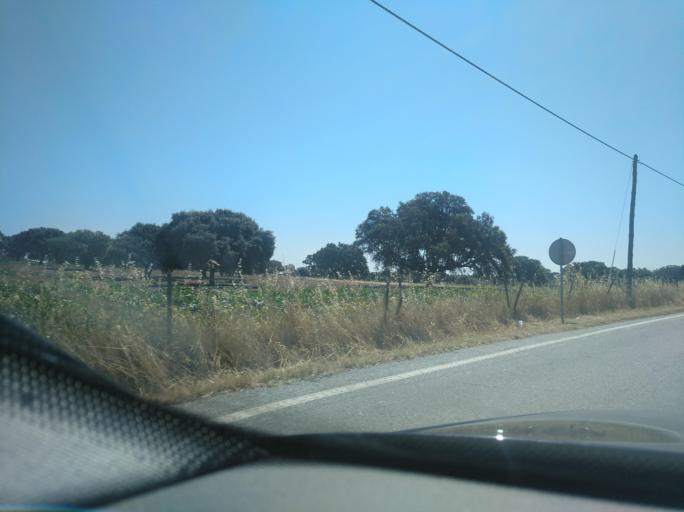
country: PT
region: Portalegre
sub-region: Arronches
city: Arronches
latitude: 38.9928
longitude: -7.3426
